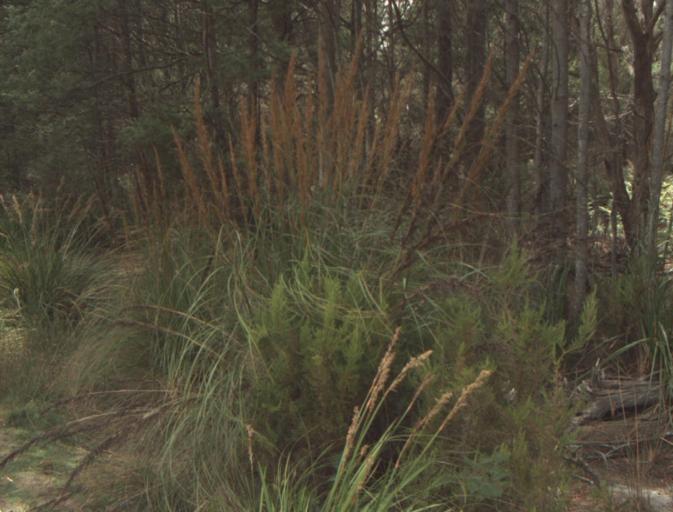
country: AU
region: Tasmania
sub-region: Launceston
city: Mayfield
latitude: -41.2684
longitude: 147.1650
